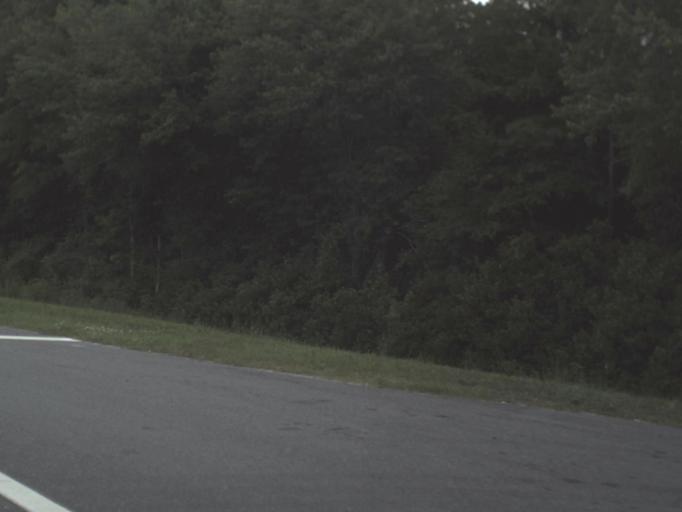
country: US
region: Florida
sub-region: Columbia County
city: Five Points
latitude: 30.2440
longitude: -82.6383
